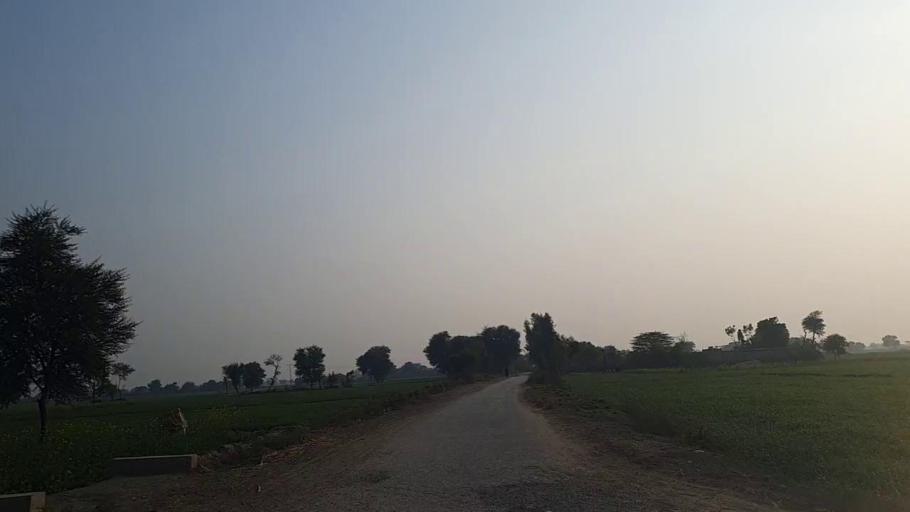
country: PK
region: Sindh
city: Nawabshah
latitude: 26.2141
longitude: 68.4724
